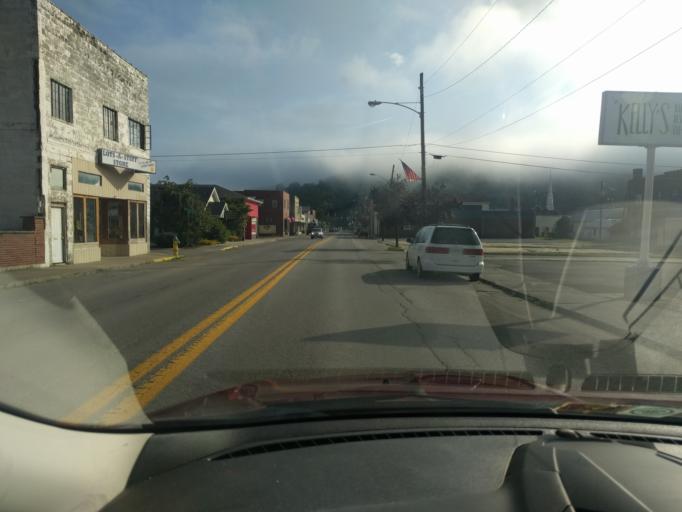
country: US
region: West Virginia
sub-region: Greenbrier County
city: Rainelle
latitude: 37.9705
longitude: -80.7642
